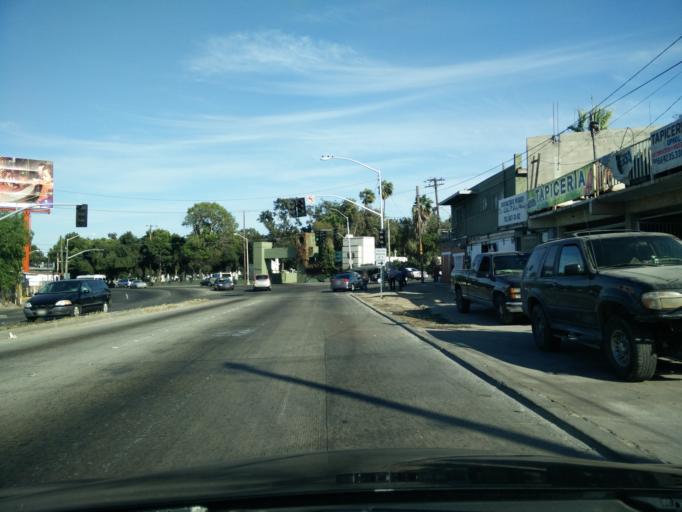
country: MX
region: Baja California
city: Tijuana
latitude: 32.5319
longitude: -117.0636
